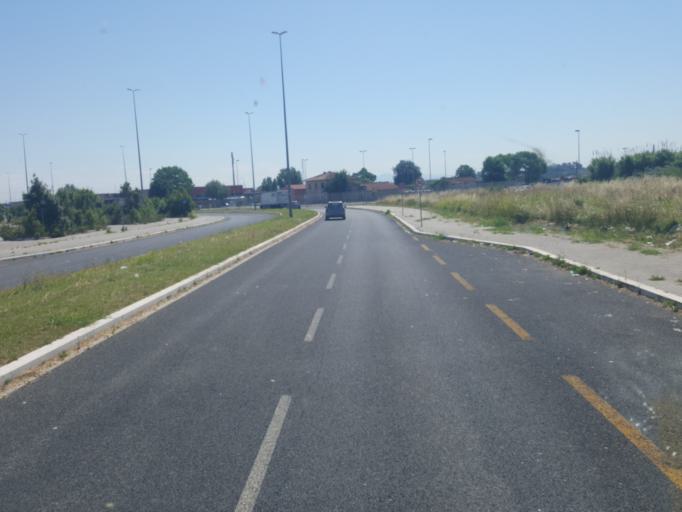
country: IT
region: Latium
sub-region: Citta metropolitana di Roma Capitale
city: Npp 23 (Parco Leonardo)
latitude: 41.8016
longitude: 12.3189
